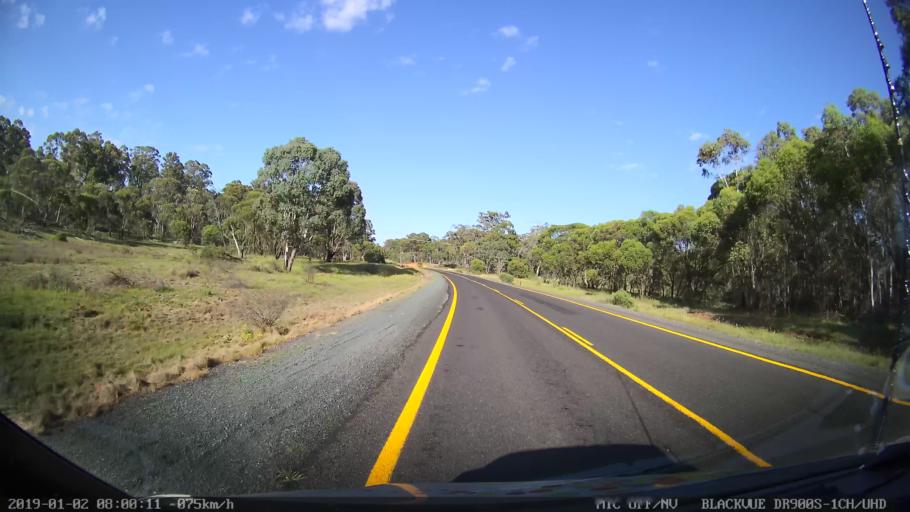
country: AU
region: New South Wales
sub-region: Tumut Shire
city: Tumut
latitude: -35.6439
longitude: 148.4489
